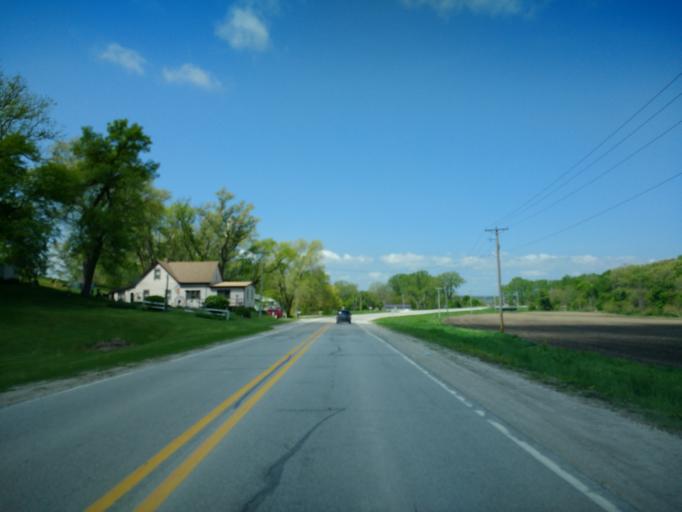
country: US
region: Iowa
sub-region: Harrison County
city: Missouri Valley
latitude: 41.4326
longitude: -95.8628
